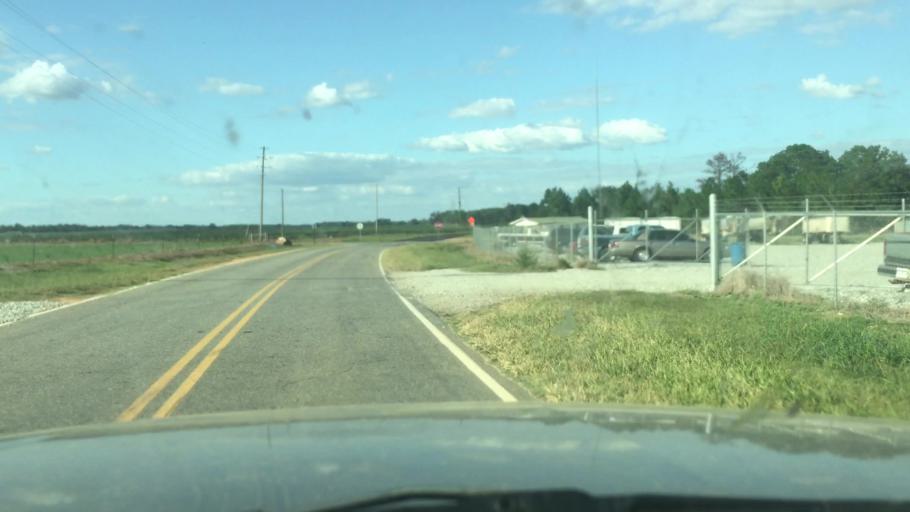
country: US
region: Georgia
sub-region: Terrell County
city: Dawson
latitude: 31.7649
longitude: -84.3538
